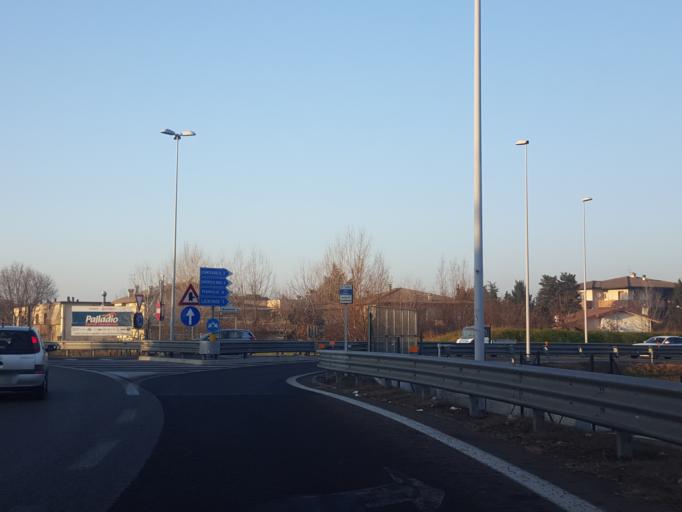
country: IT
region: Veneto
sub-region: Provincia di Vicenza
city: Torri di Quartesolo
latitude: 45.5130
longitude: 11.6265
